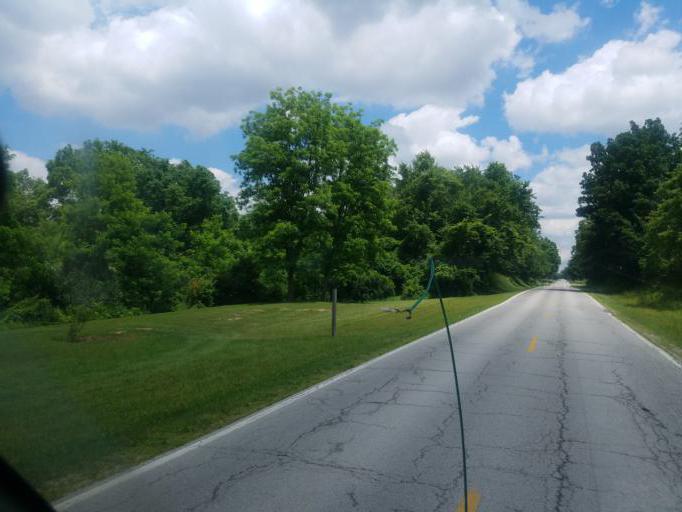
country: US
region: Ohio
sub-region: Huron County
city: Willard
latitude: 41.0692
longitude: -82.7510
